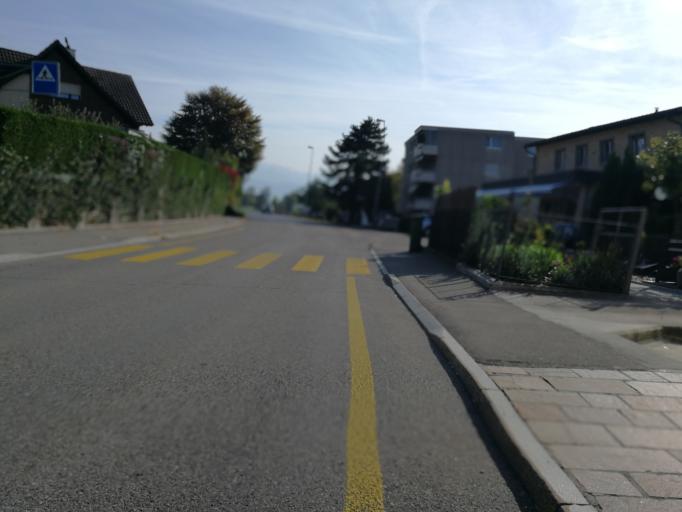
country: CH
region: Zurich
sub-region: Bezirk Hinwil
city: Hadlikon
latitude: 47.2875
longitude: 8.8564
